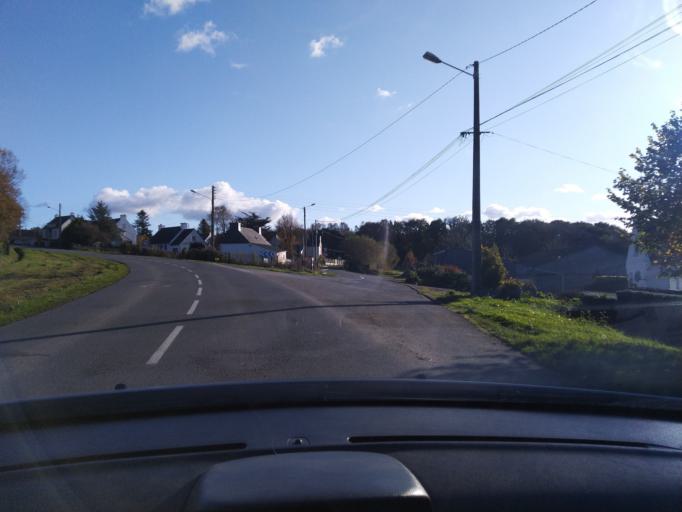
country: FR
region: Brittany
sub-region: Departement des Cotes-d'Armor
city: Plestin-les-Greves
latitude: 48.6442
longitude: -3.6284
